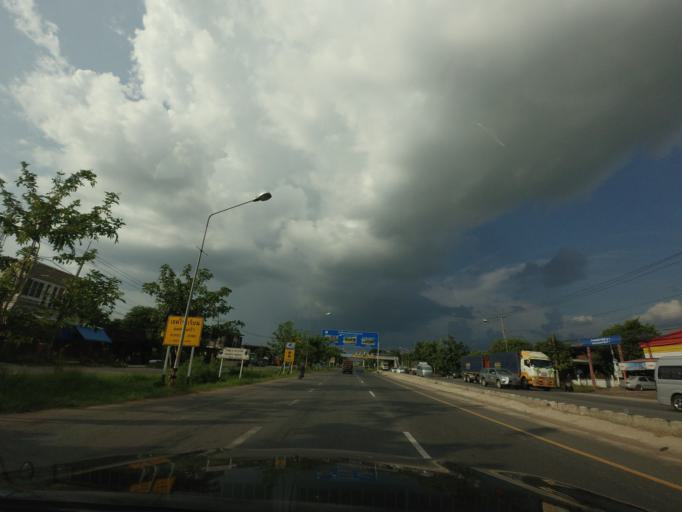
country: TH
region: Khon Kaen
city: Khon Kaen
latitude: 16.3250
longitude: 102.7965
